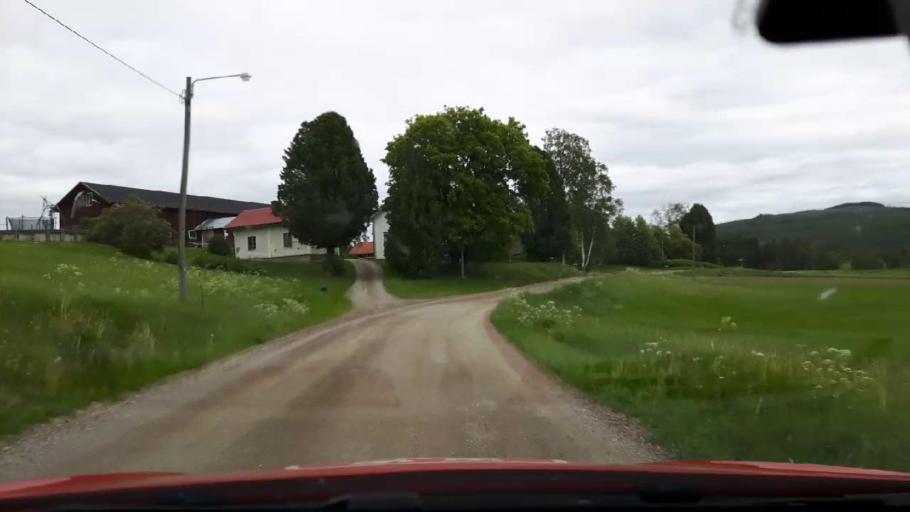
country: SE
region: Jaemtland
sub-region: Ragunda Kommun
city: Hammarstrand
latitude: 63.1580
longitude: 16.2351
